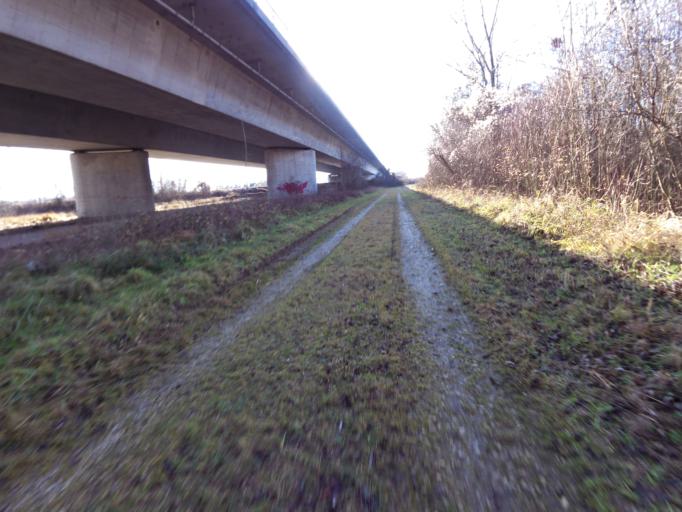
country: DE
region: Bavaria
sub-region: Lower Bavaria
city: Bruckberg
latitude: 48.4962
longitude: 12.0045
